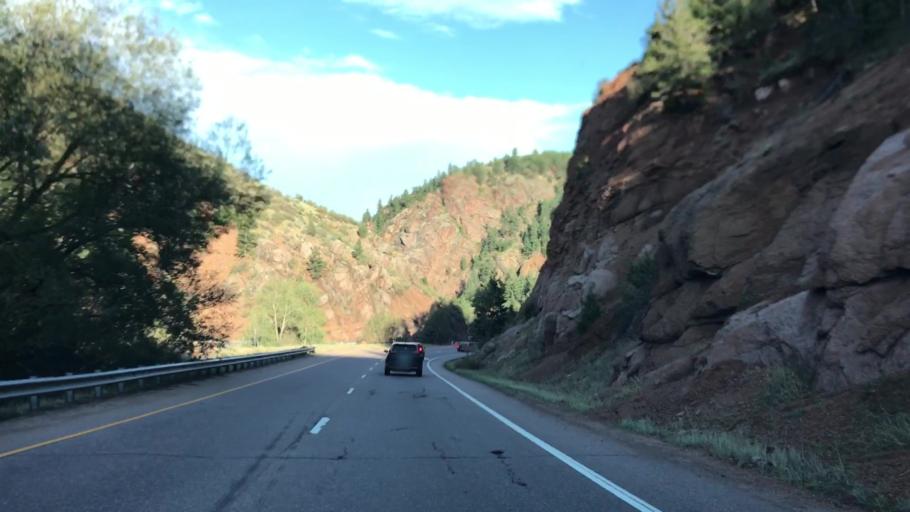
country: US
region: Colorado
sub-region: El Paso County
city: Manitou Springs
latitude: 38.8772
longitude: -104.9394
